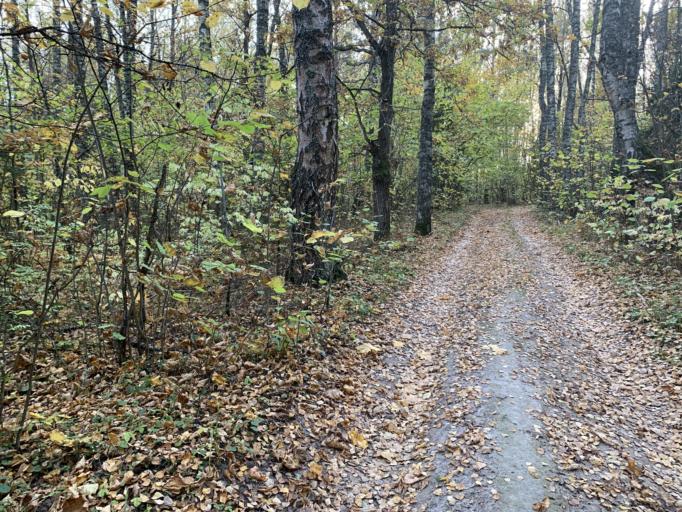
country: RU
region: Jaroslavl
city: Petrovsk
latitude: 56.9840
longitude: 39.3780
